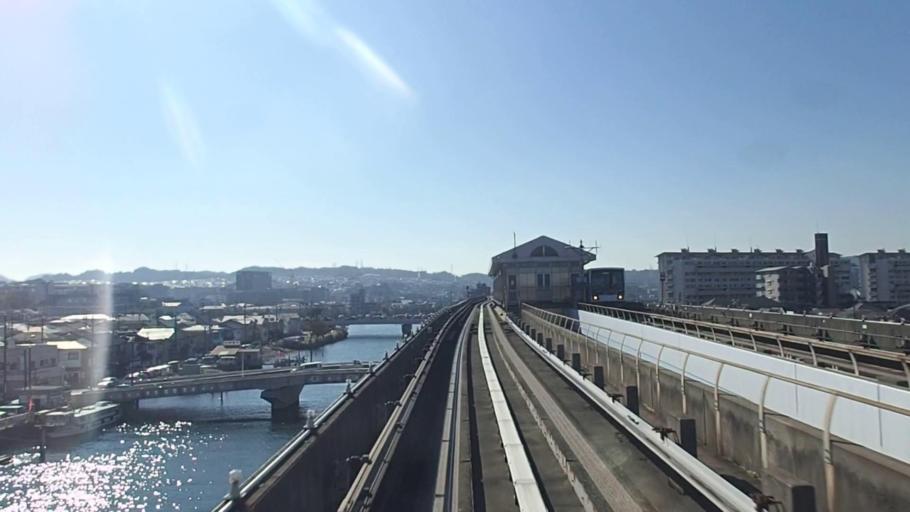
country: JP
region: Kanagawa
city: Yokosuka
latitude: 35.3309
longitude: 139.6323
